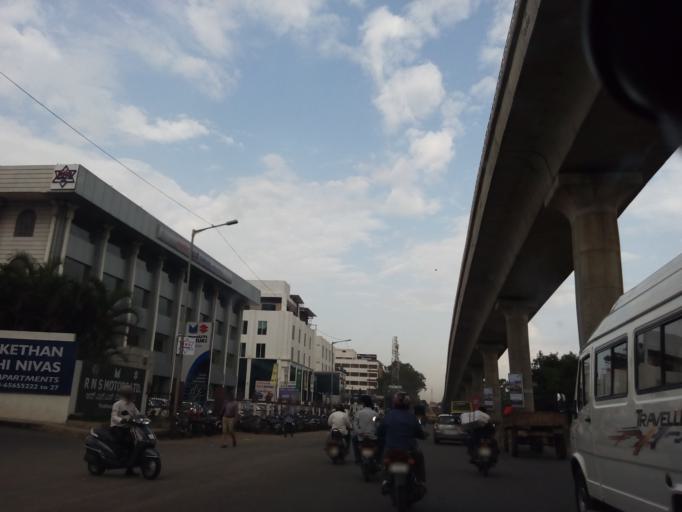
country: IN
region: Karnataka
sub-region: Bangalore Urban
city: Bangalore
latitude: 13.0280
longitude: 77.5418
